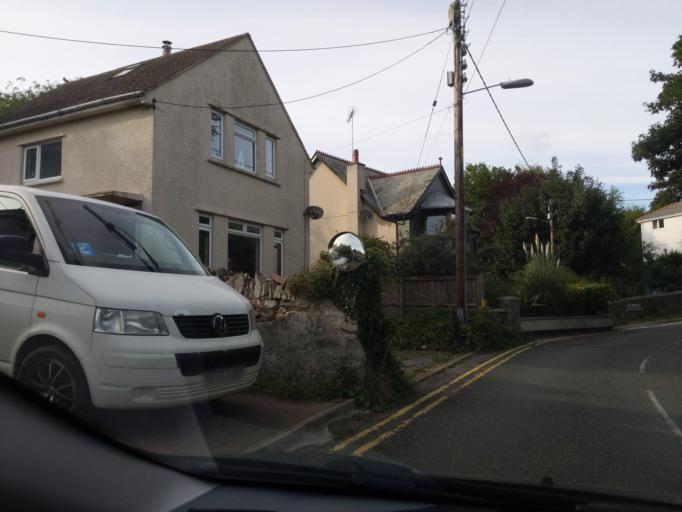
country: GB
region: England
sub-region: Cornwall
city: Millbrook
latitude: 50.3351
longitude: -4.2040
